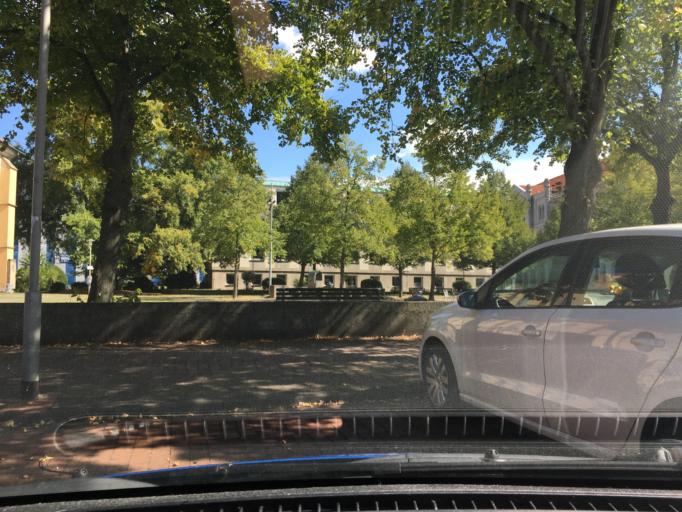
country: DE
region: Lower Saxony
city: Hannover
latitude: 52.3709
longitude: 9.7281
